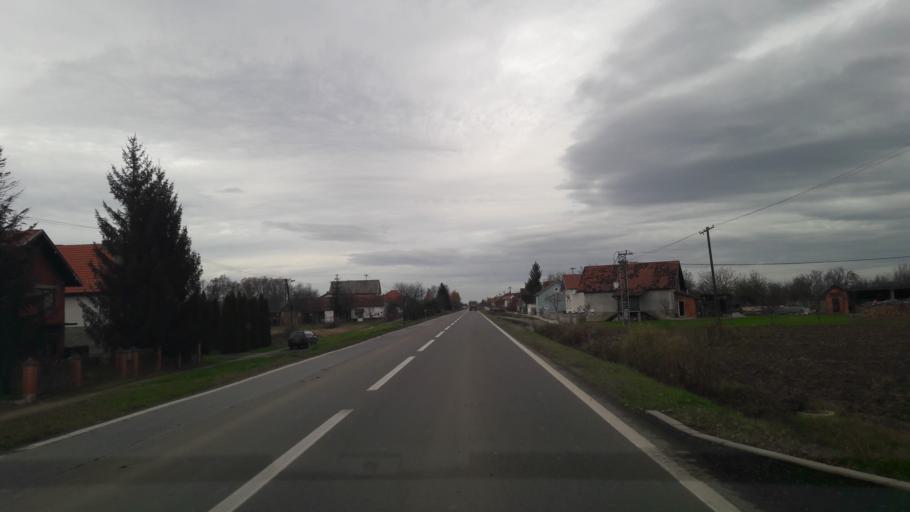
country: HR
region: Osjecko-Baranjska
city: Fericanci
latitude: 45.5272
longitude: 17.9597
